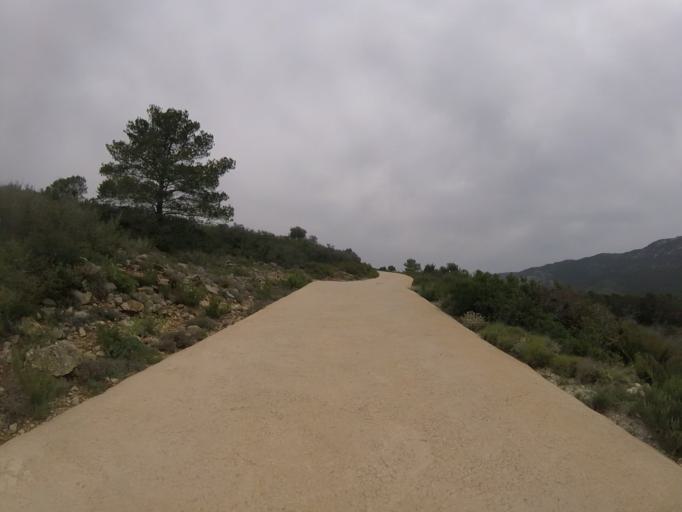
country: ES
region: Valencia
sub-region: Provincia de Castello
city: Alcala de Xivert
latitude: 40.2963
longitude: 0.2565
